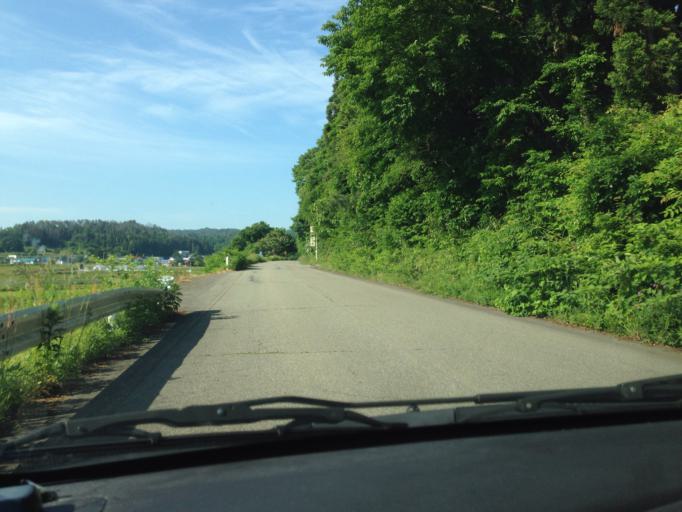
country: JP
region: Fukushima
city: Kitakata
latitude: 37.5137
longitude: 139.8075
